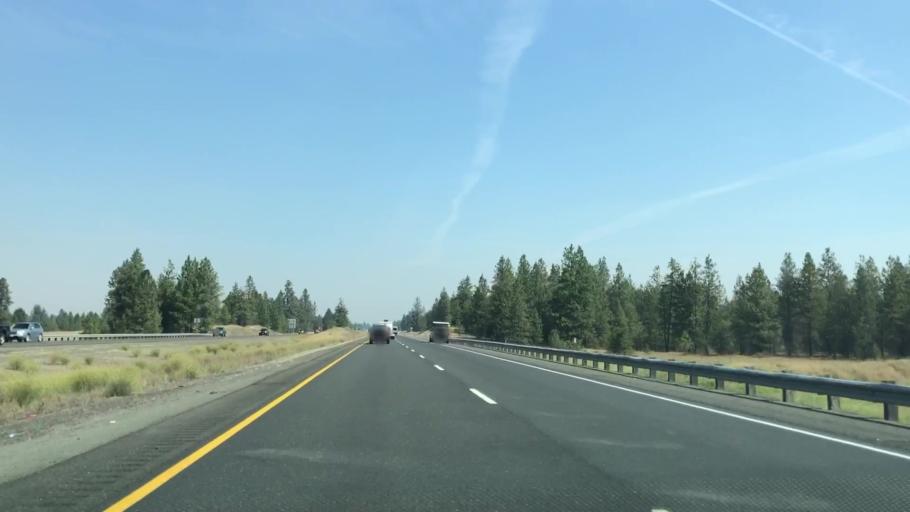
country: US
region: Washington
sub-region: Spokane County
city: Medical Lake
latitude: 47.4468
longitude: -117.7747
